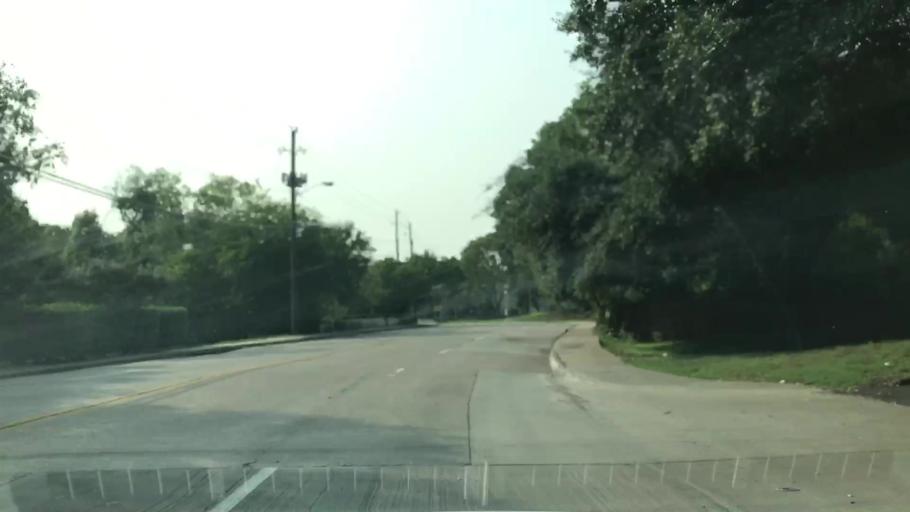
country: US
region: Texas
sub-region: Dallas County
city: Richardson
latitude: 32.9003
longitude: -96.7253
